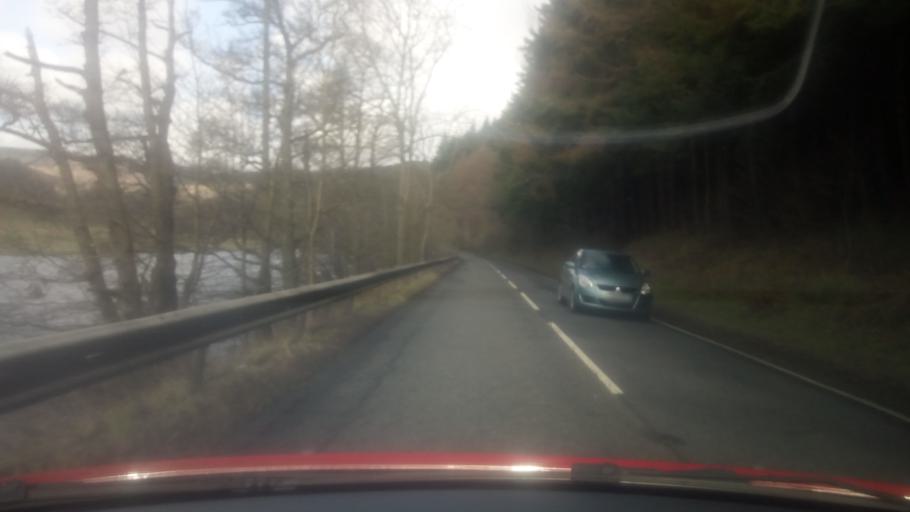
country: GB
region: Scotland
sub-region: The Scottish Borders
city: Innerleithen
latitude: 55.6221
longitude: -2.9572
